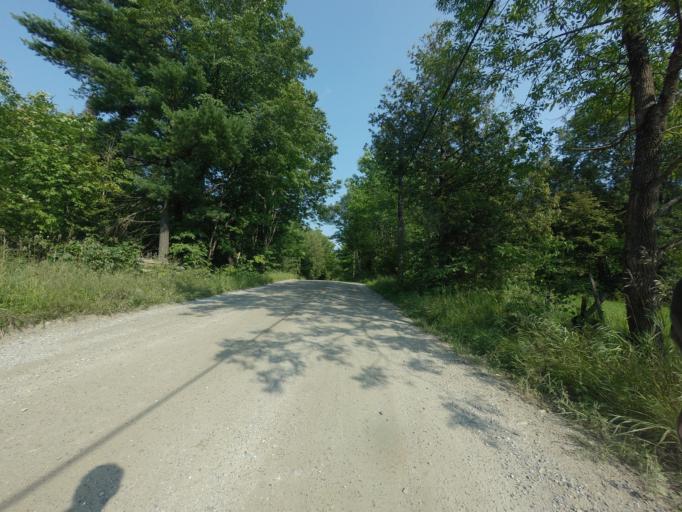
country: CA
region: Ontario
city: Perth
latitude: 44.8034
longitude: -76.7298
